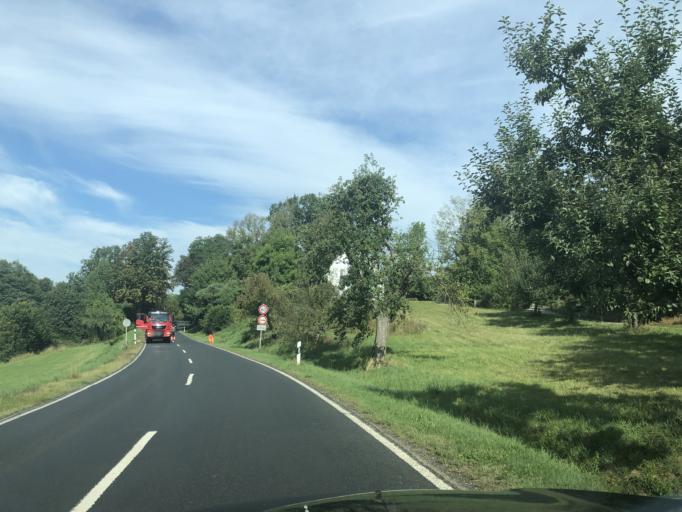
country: DE
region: Bavaria
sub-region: Upper Palatinate
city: Pressath
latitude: 49.7759
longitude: 11.9289
